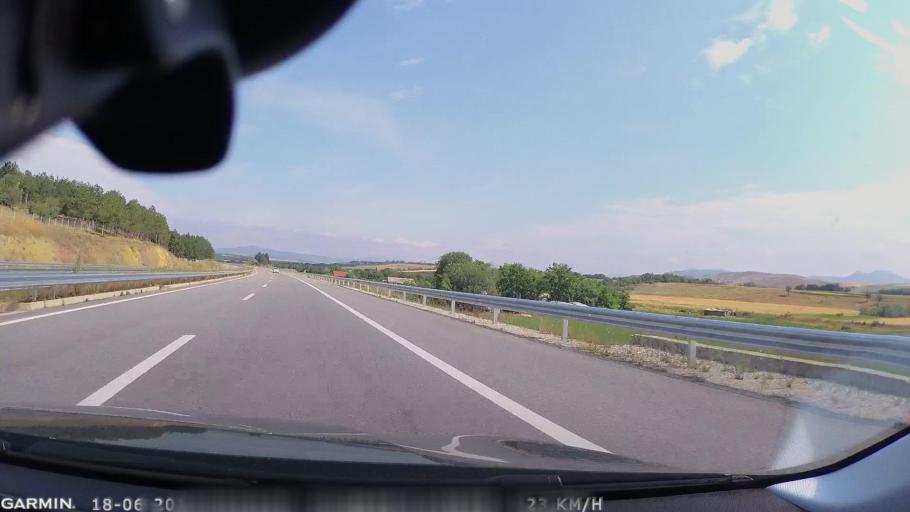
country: MK
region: Sveti Nikole
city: Sveti Nikole
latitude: 41.8853
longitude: 21.9334
